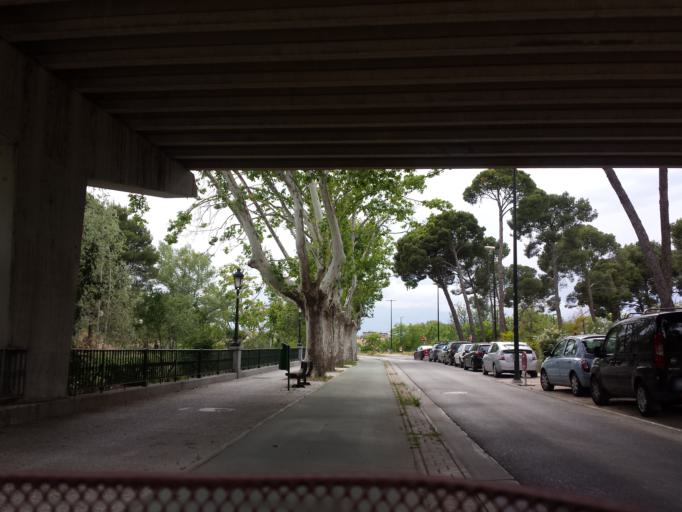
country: ES
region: Aragon
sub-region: Provincia de Zaragoza
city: Delicias
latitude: 41.6297
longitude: -0.8949
